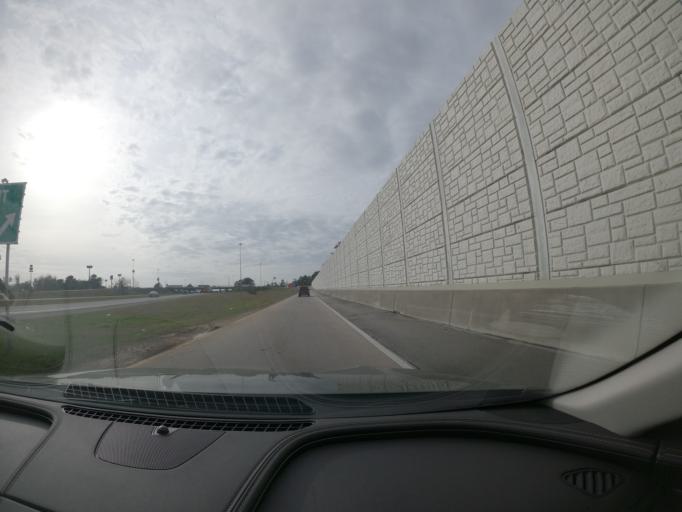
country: US
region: Georgia
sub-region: Columbia County
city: Evans
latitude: 33.4837
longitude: -82.1284
